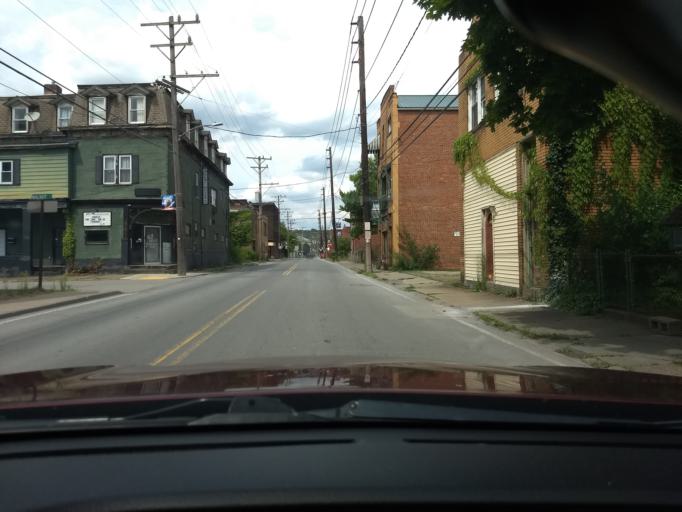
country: US
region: Pennsylvania
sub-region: Allegheny County
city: Brackenridge
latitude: 40.6114
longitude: -79.7215
